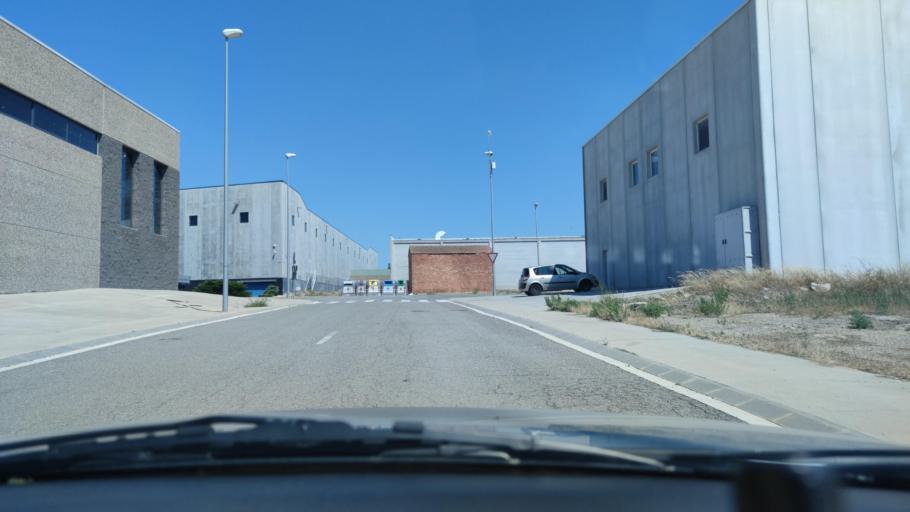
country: ES
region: Catalonia
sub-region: Provincia de Lleida
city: Torrefarrera
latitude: 41.6798
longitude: 0.6287
